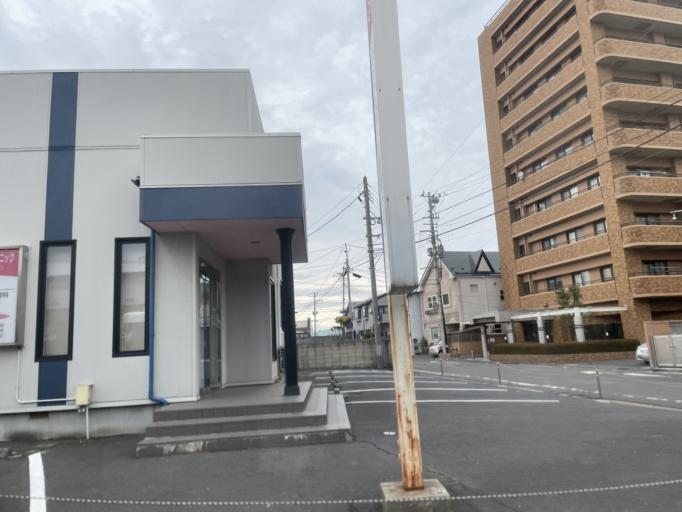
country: JP
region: Aomori
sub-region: Hachinohe Shi
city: Uchimaru
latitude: 40.5056
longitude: 141.4844
